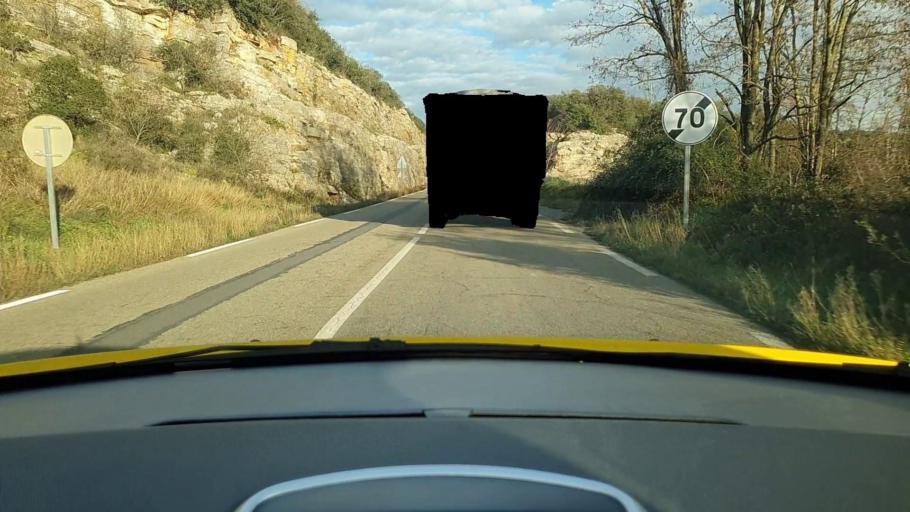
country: FR
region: Languedoc-Roussillon
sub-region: Departement du Gard
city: Saint-Martin-de-Valgalgues
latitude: 44.1733
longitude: 4.0821
